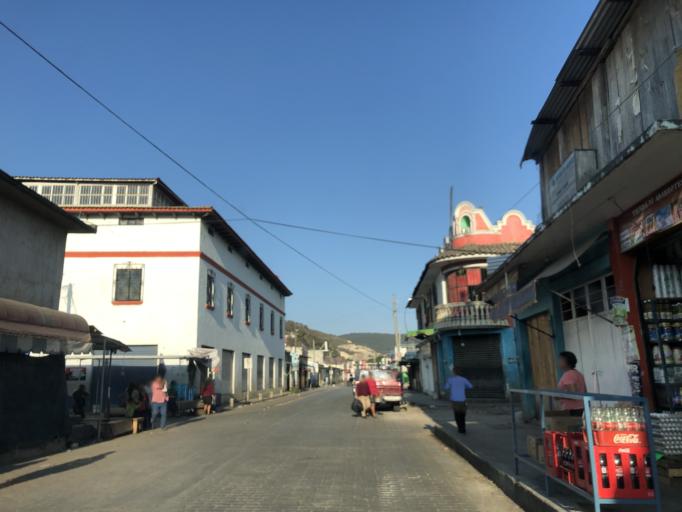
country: MX
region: Chiapas
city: San Cristobal de las Casas
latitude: 16.7188
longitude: -92.6390
